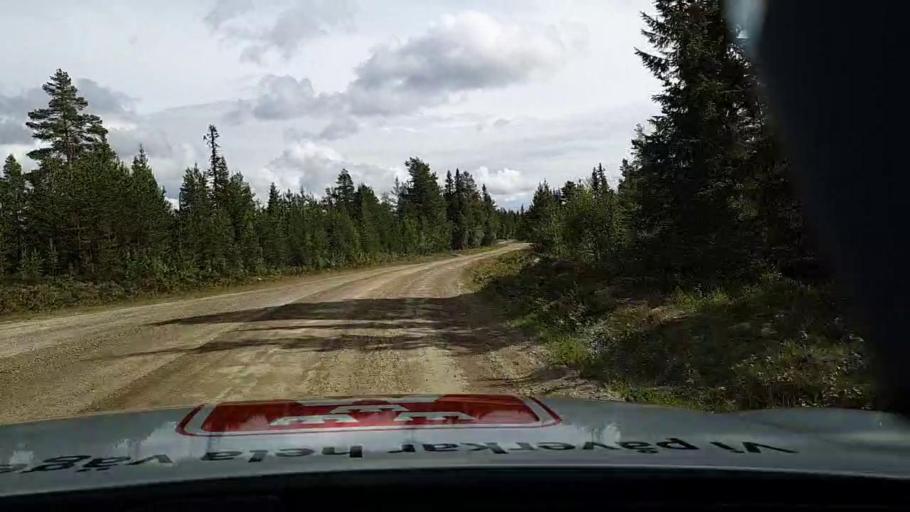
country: SE
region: Jaemtland
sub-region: Are Kommun
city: Jarpen
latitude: 62.5464
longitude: 13.4706
